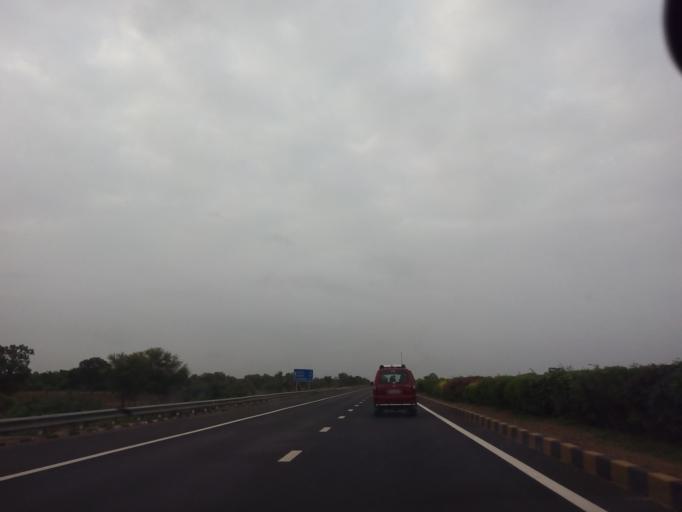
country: IN
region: Gujarat
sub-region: Kheda
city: Nadiad
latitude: 22.7810
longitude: 72.8465
